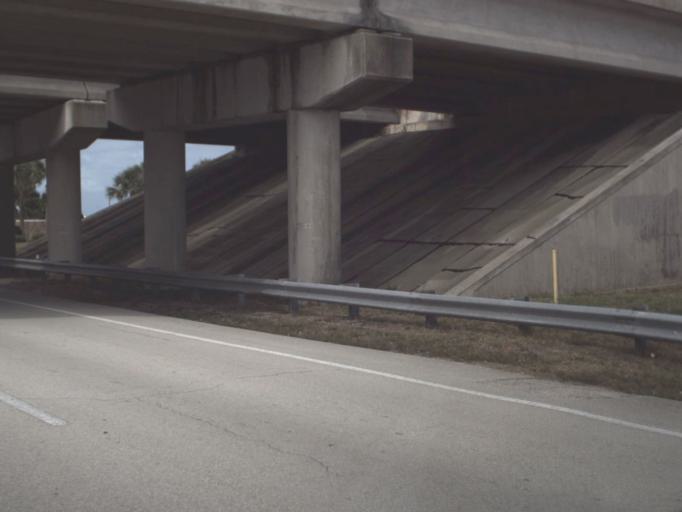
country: US
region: Florida
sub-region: Brevard County
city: South Patrick Shores
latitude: 28.2125
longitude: -80.6065
